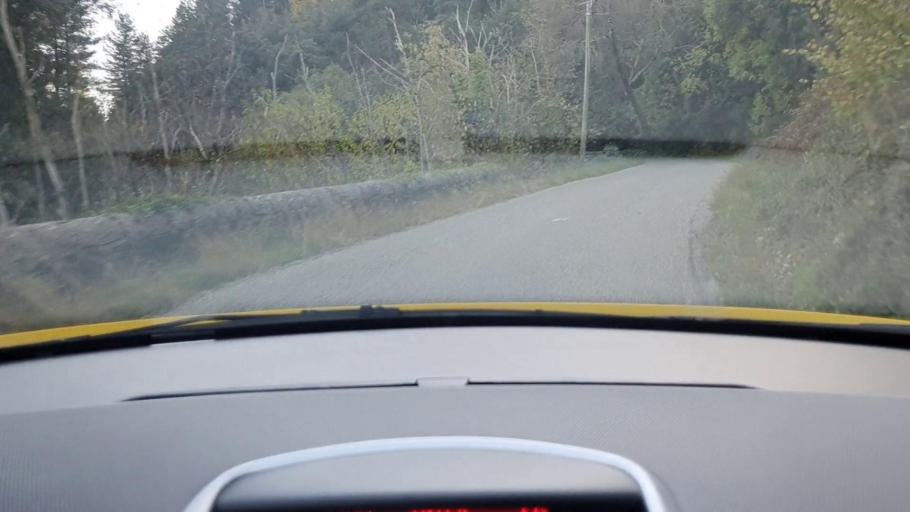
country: FR
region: Languedoc-Roussillon
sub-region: Departement du Gard
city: Sumene
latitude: 43.9794
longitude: 3.6785
